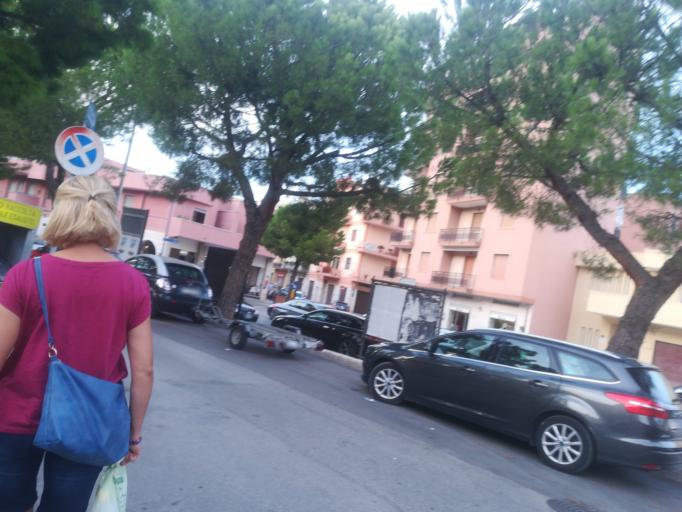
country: IT
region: Apulia
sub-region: Provincia di Bari
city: Monopoli
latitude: 40.9464
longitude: 17.3041
